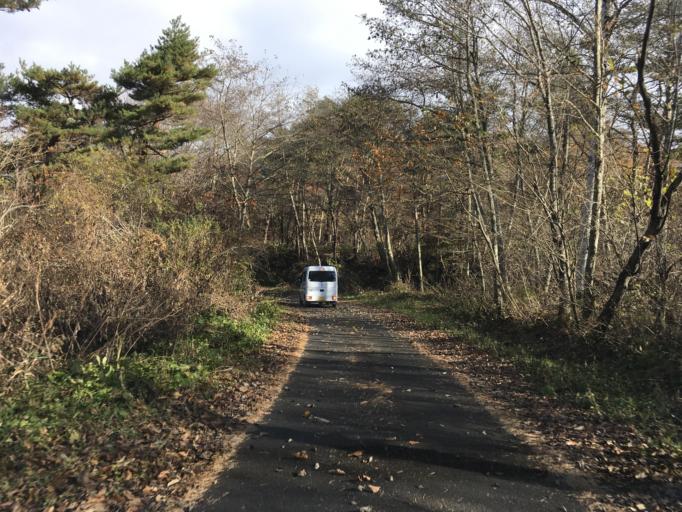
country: JP
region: Iwate
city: Mizusawa
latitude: 39.1255
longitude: 141.3028
